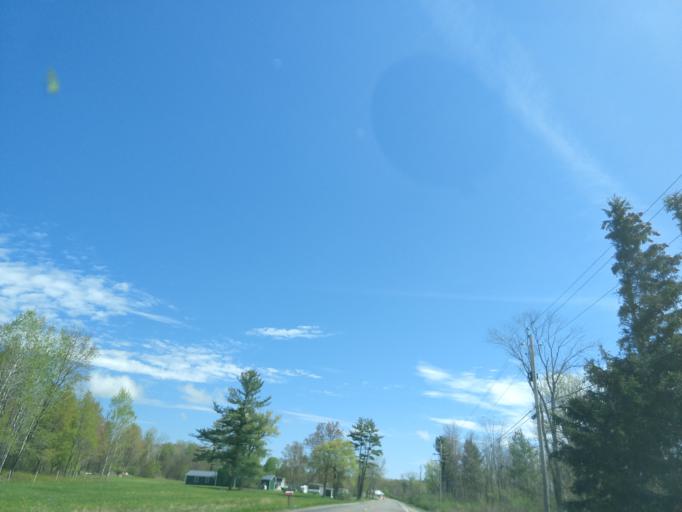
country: US
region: New York
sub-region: Tompkins County
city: Dryden
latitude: 42.4997
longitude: -76.3659
